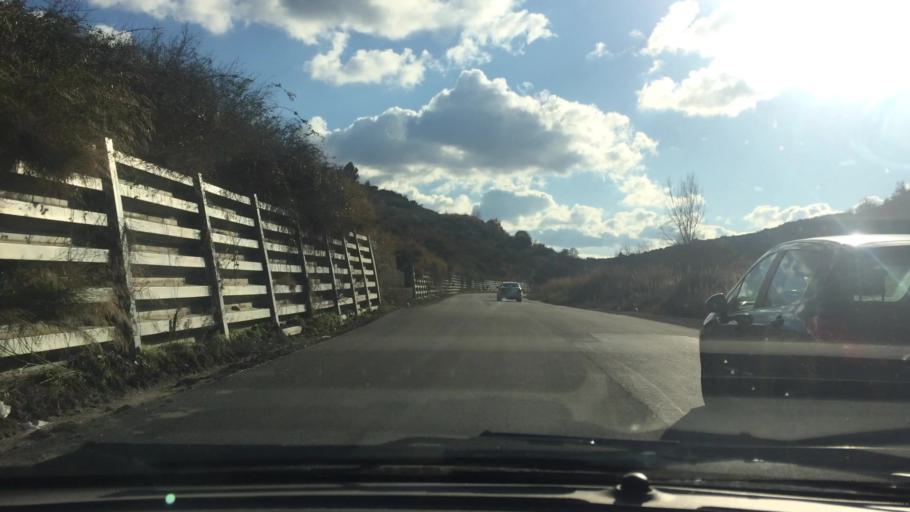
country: IT
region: Basilicate
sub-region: Provincia di Potenza
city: Tolve
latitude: 40.7213
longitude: 16.0360
